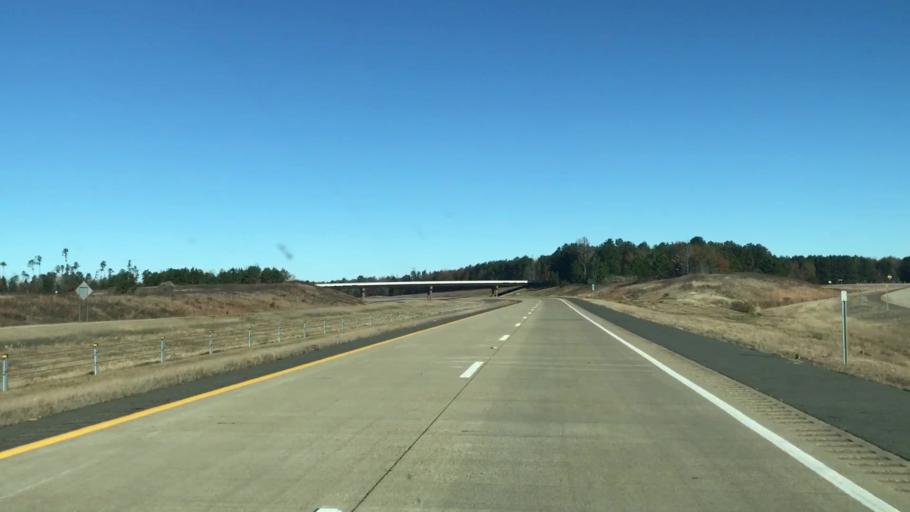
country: US
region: Texas
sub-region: Bowie County
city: Texarkana
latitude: 33.2657
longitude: -93.8975
